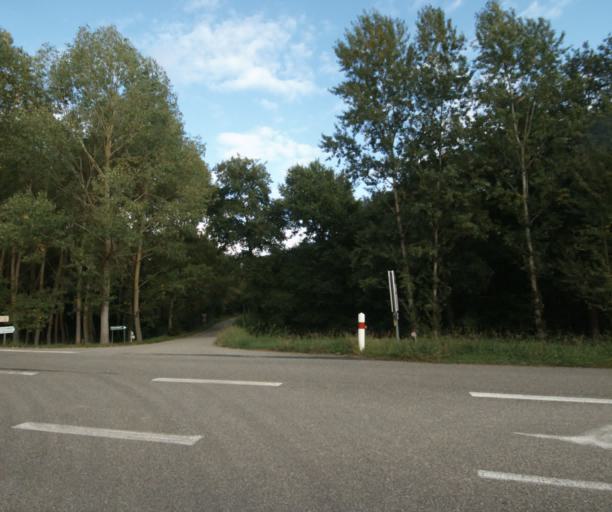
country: FR
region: Midi-Pyrenees
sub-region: Departement du Gers
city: Eauze
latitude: 43.8992
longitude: 0.0988
